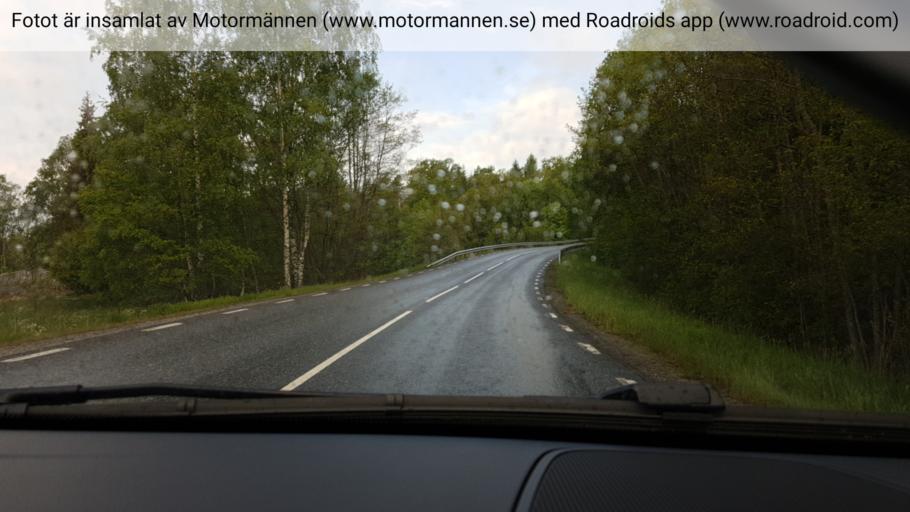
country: SE
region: Stockholm
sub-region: Nynashamns Kommun
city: Nynashamn
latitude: 58.9554
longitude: 17.9672
